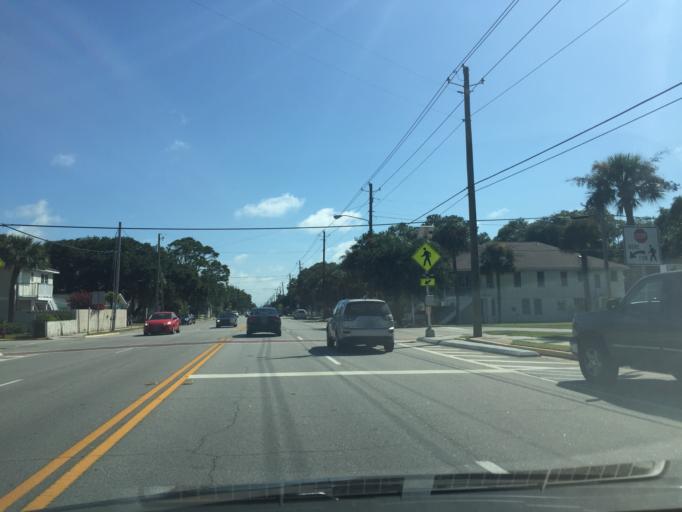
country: US
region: Georgia
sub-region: Chatham County
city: Tybee Island
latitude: 32.0013
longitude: -80.8457
